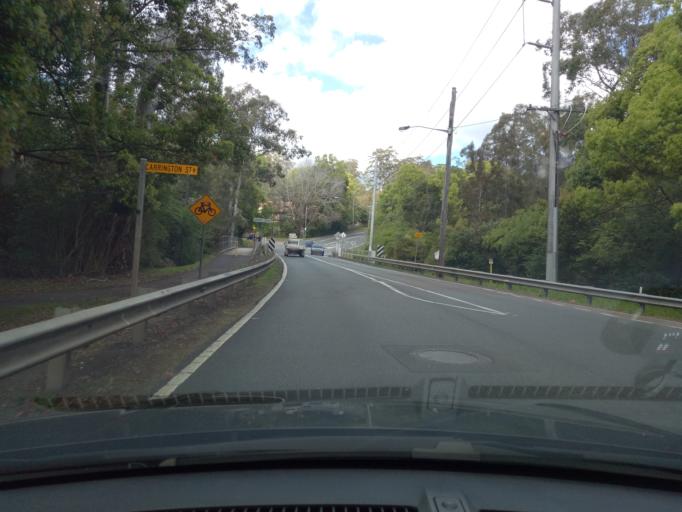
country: AU
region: New South Wales
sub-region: Gosford Shire
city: Narara
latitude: -33.4011
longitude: 151.3426
